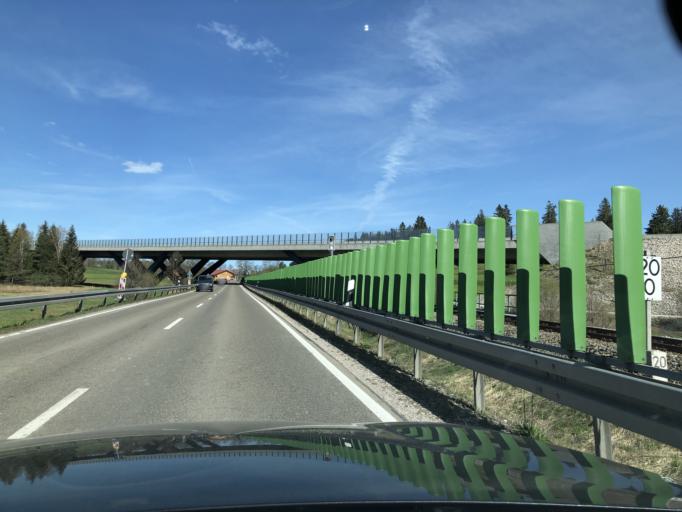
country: DE
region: Bavaria
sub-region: Swabia
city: Eisenberg
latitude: 47.6284
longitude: 10.6025
